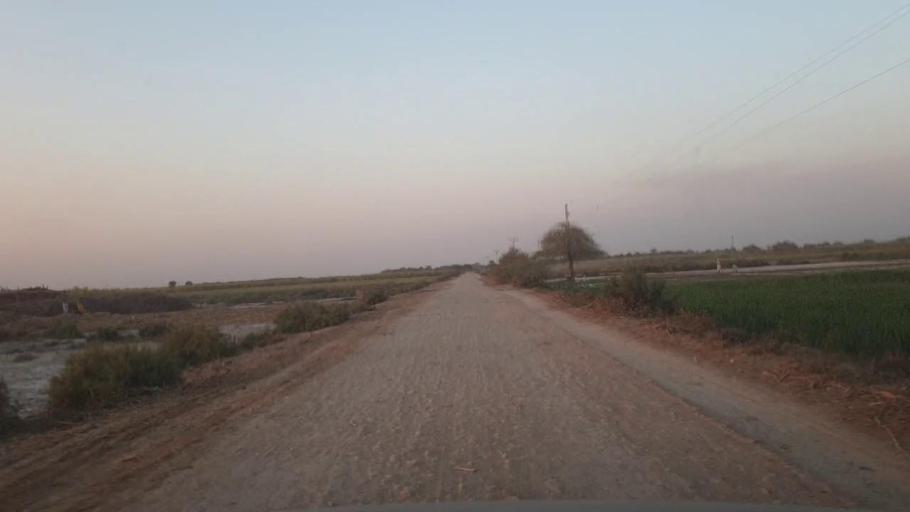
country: PK
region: Sindh
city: Chambar
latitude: 25.3044
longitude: 68.9075
